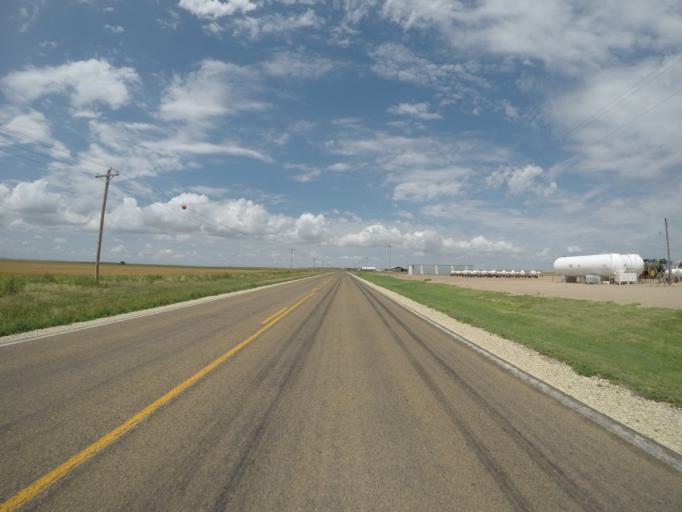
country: US
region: Kansas
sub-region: Rawlins County
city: Atwood
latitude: 39.8325
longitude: -101.0468
